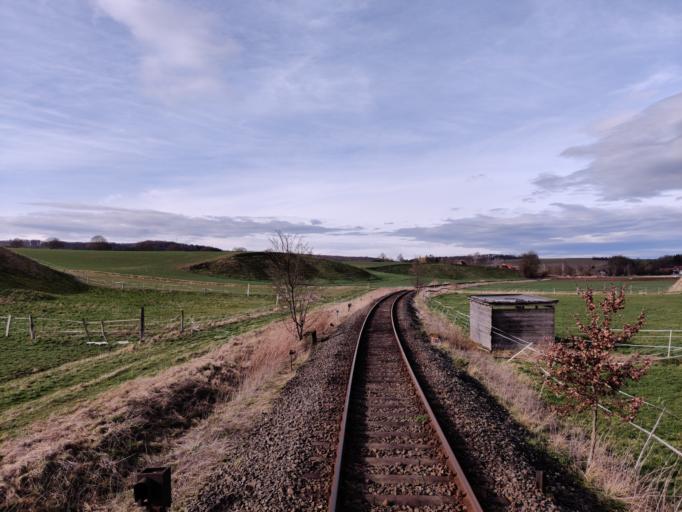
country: DE
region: Lower Saxony
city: Bockenem
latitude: 51.9769
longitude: 10.1257
